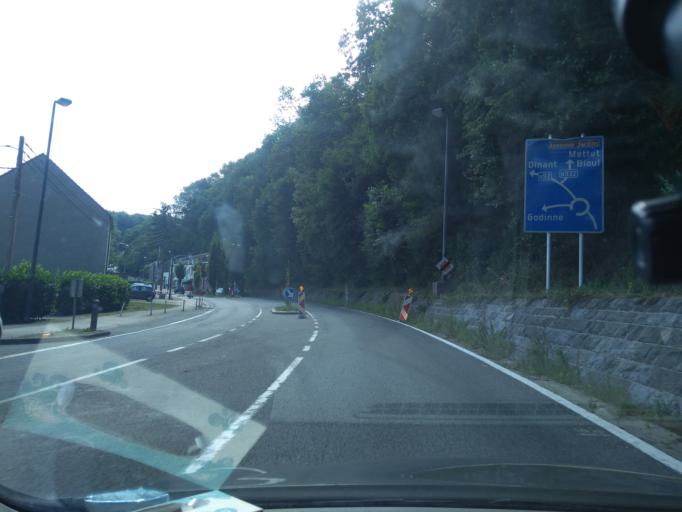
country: BE
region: Wallonia
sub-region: Province de Namur
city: Profondeville
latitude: 50.3499
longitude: 4.8520
